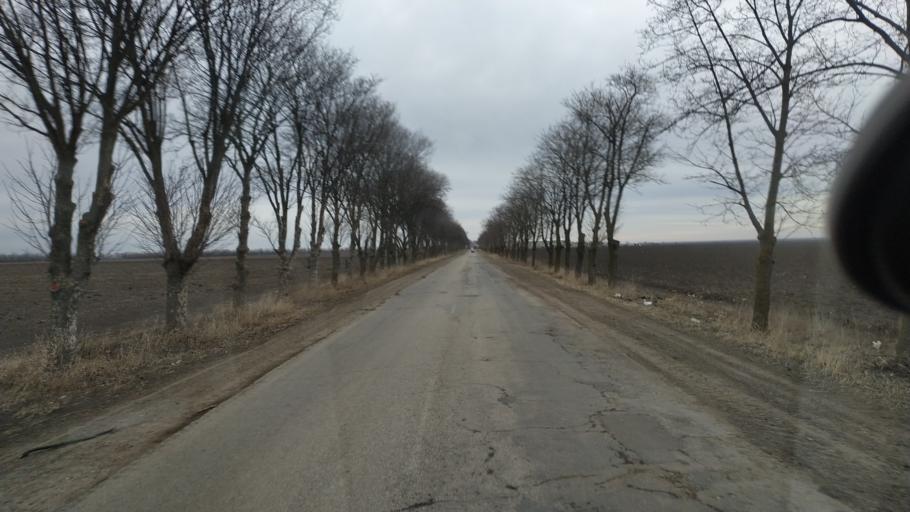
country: MD
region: Telenesti
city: Cocieri
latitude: 47.2660
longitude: 29.0913
